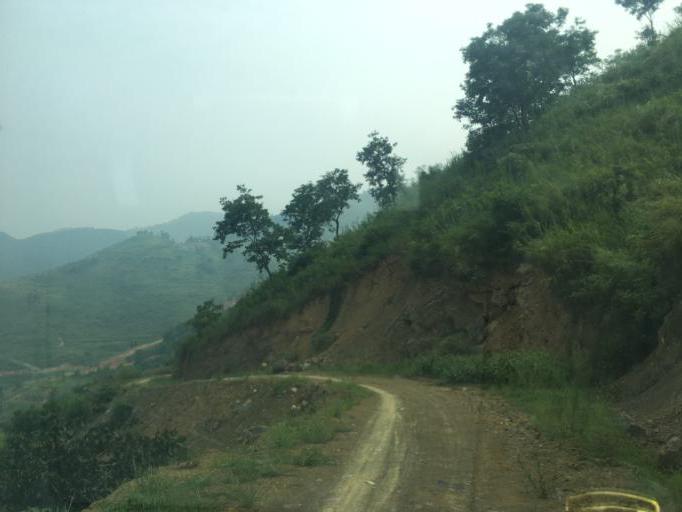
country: CN
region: Guizhou Sheng
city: Anshun
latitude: 25.4545
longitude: 105.9388
